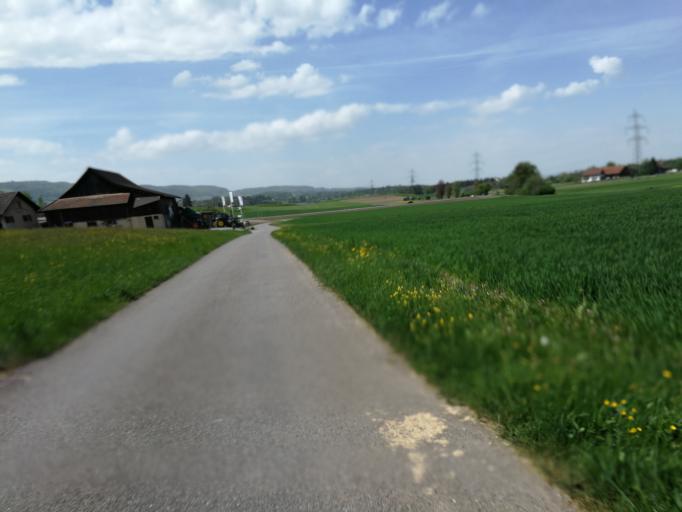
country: CH
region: Zurich
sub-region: Bezirk Meilen
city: Oetwil am See
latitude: 47.2827
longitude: 8.7335
